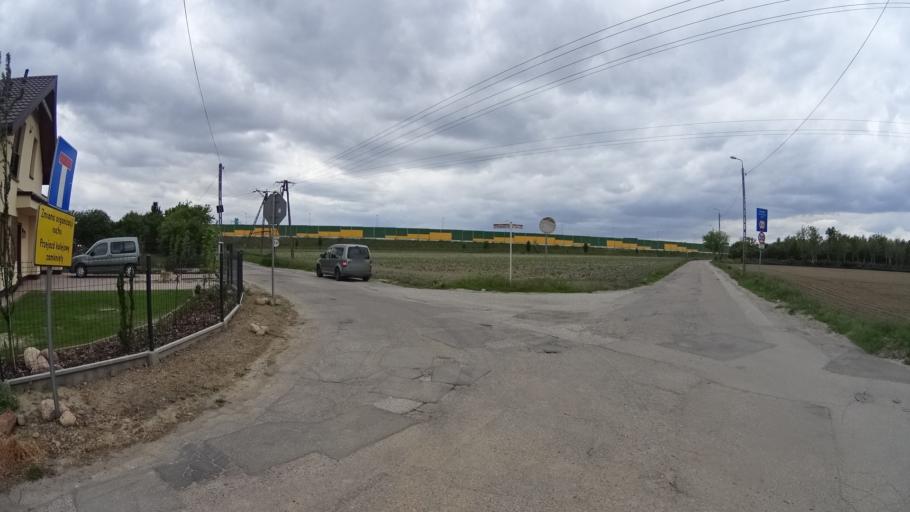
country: PL
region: Masovian Voivodeship
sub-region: Warszawa
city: Ursus
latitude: 52.2096
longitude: 20.8598
